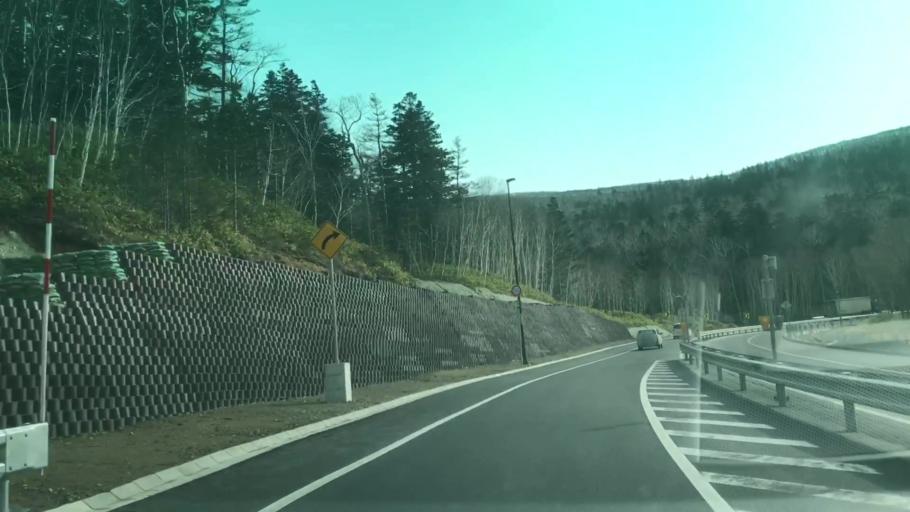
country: JP
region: Hokkaido
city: Otofuke
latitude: 42.9836
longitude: 142.7539
